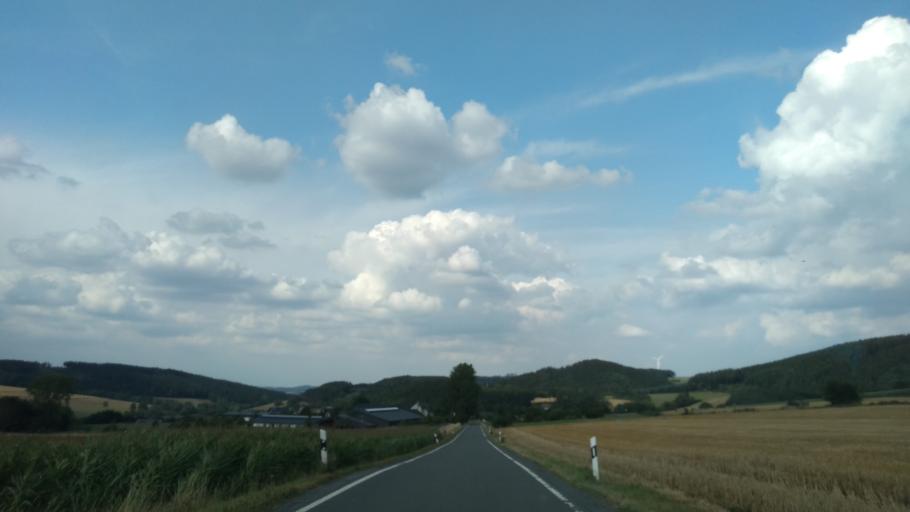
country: DE
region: North Rhine-Westphalia
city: Plettenberg
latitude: 51.2655
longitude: 7.8719
